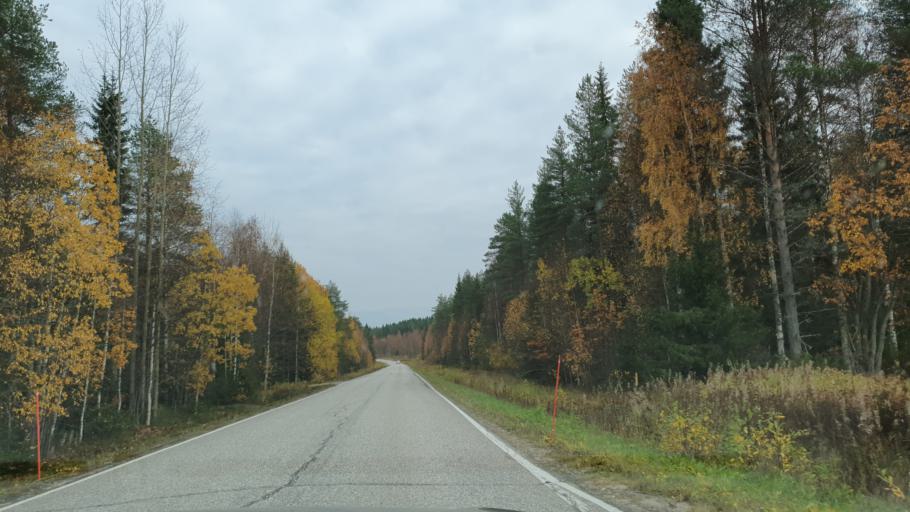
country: FI
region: Kainuu
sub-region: Kajaani
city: Ristijaervi
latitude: 64.4564
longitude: 28.3319
